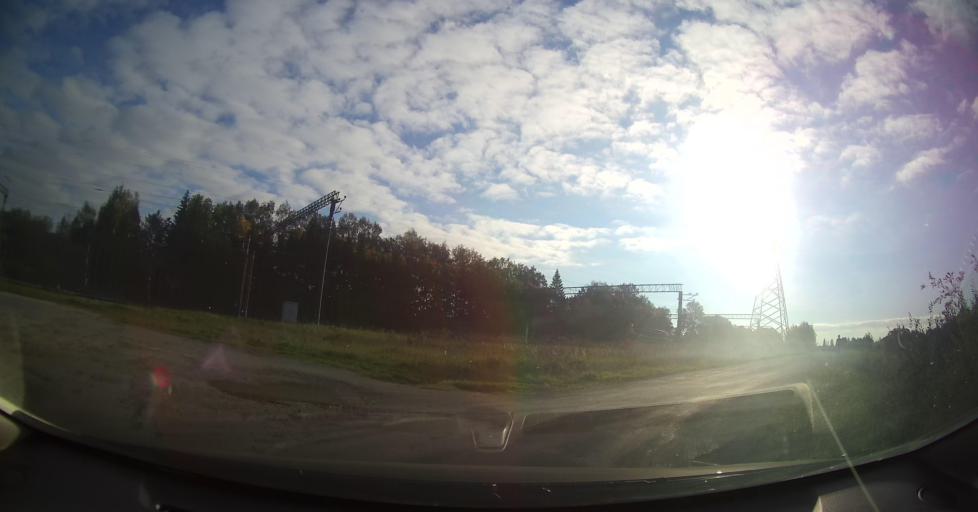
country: EE
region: Harju
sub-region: Joelaehtme vald
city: Loo
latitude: 59.4012
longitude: 24.9250
